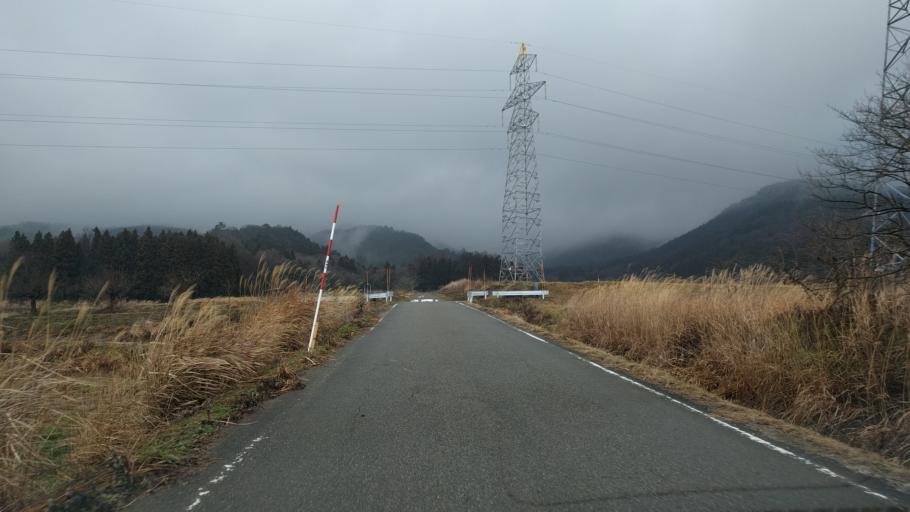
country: JP
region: Fukushima
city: Kitakata
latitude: 37.5764
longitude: 139.9615
